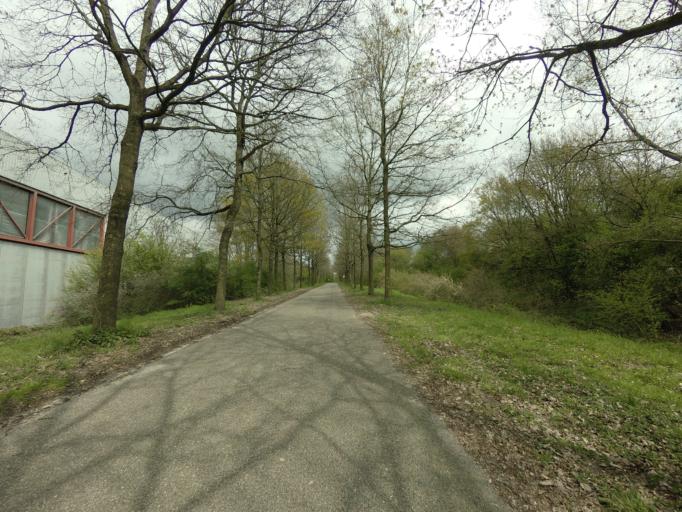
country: NL
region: Utrecht
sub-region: Gemeente Utrecht
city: Lunetten
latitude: 52.0438
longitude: 5.1107
